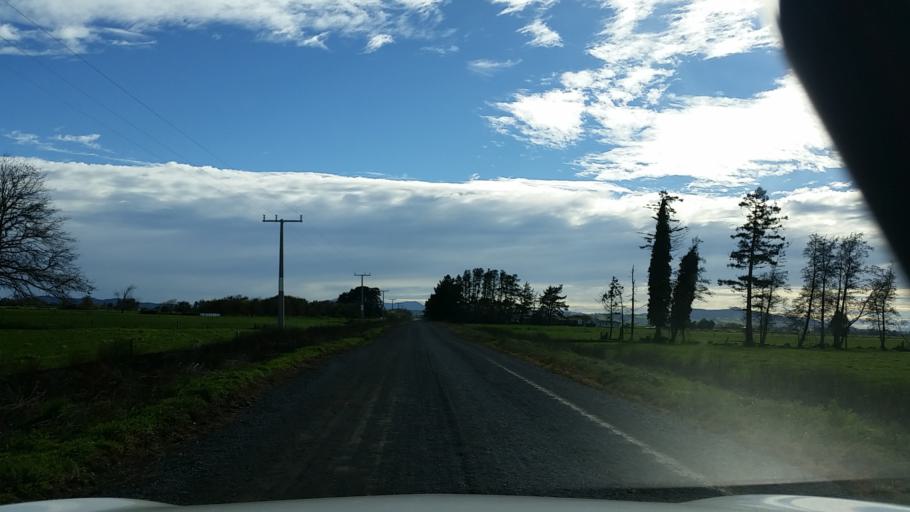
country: NZ
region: Waikato
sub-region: Hamilton City
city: Hamilton
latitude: -37.6620
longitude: 175.4376
